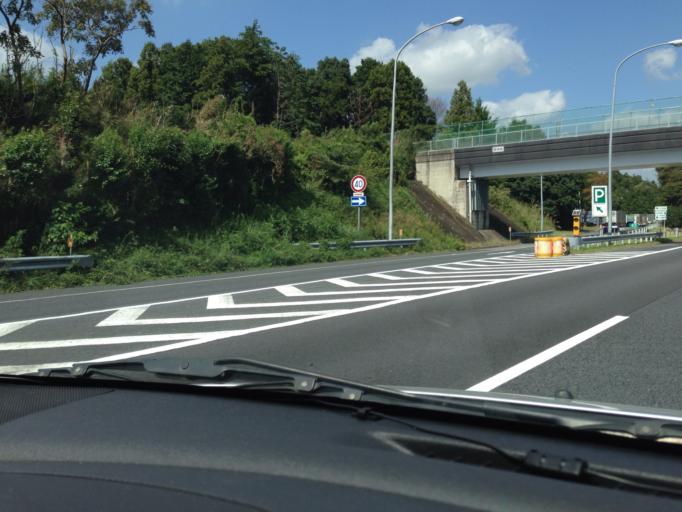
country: JP
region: Ibaraki
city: Ishioka
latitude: 36.2333
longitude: 140.2964
